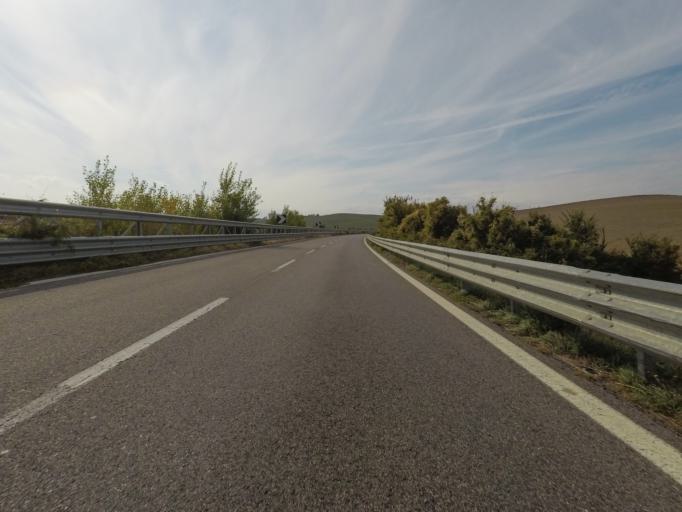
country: IT
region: Tuscany
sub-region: Provincia di Siena
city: Isola D'Arbia
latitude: 43.2591
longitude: 11.3271
